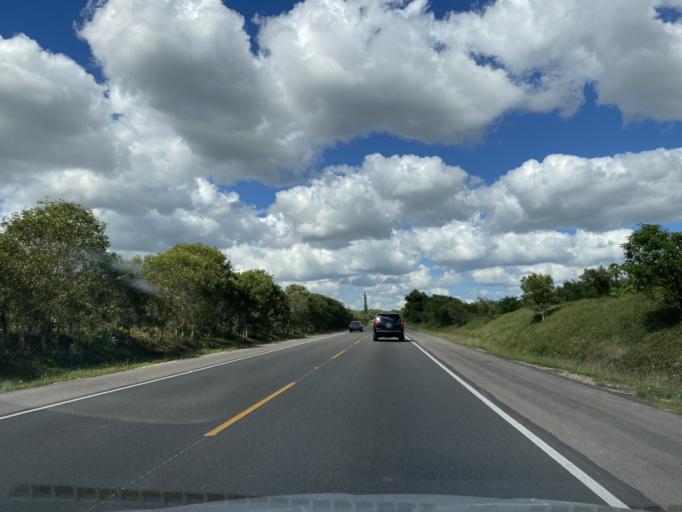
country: DO
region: Monte Plata
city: Monte Plata
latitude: 18.7398
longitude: -69.7636
